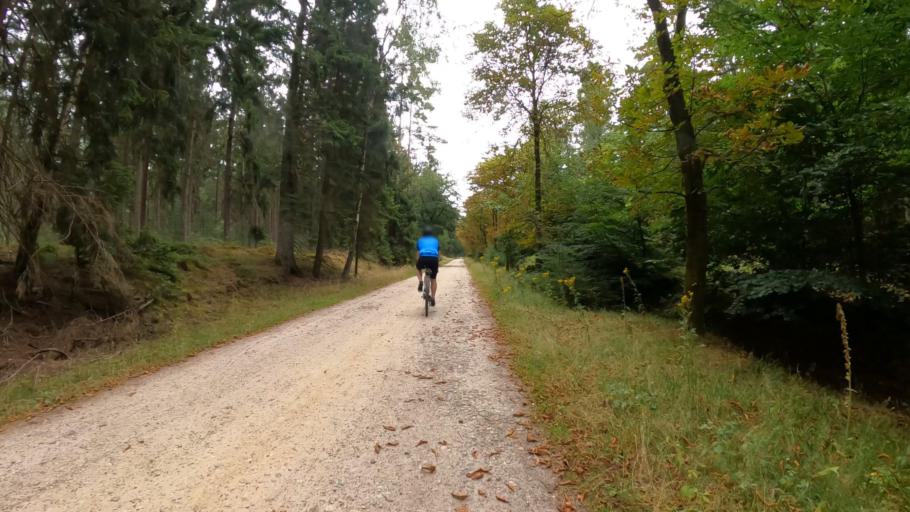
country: DE
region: Schleswig-Holstein
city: Bark
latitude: 53.9461
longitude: 10.1433
